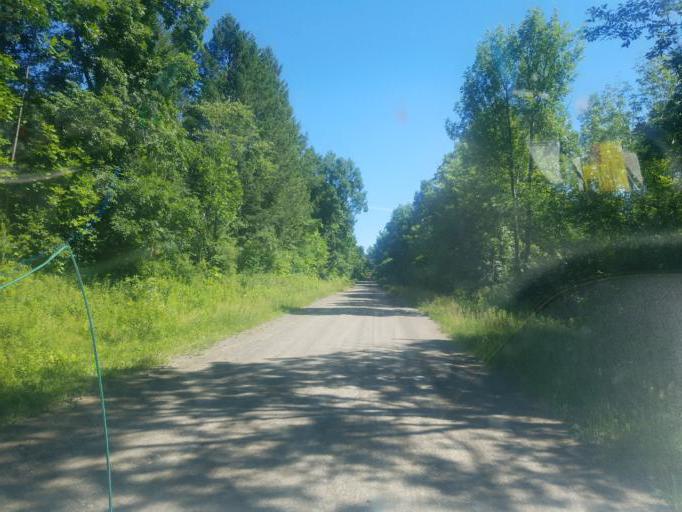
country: US
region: New York
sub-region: Ontario County
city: Naples
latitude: 42.6671
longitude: -77.3411
